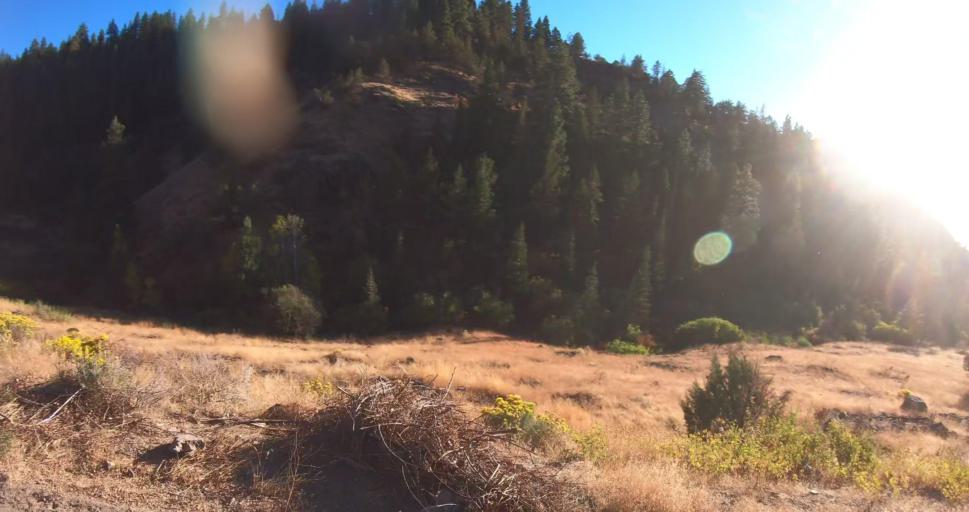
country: US
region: Oregon
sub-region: Lake County
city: Lakeview
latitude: 42.1931
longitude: -120.3158
